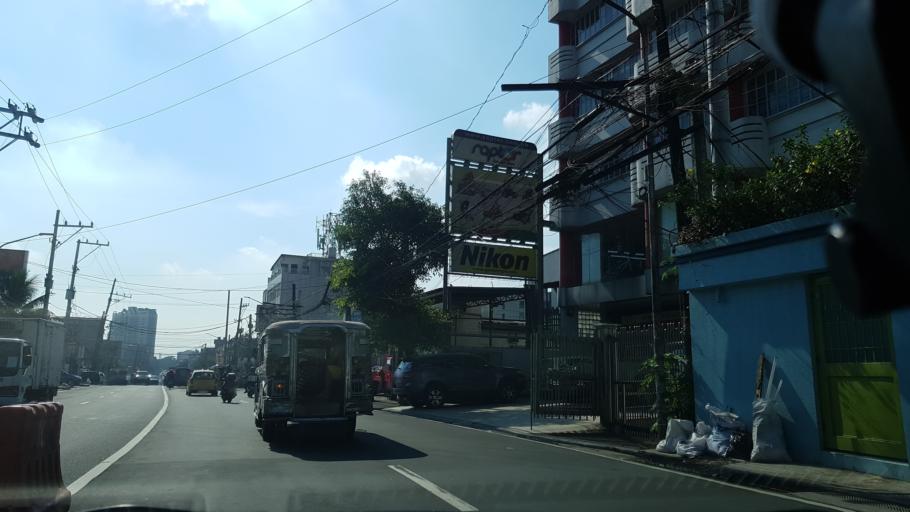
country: PH
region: Metro Manila
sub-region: San Juan
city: San Juan
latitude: 14.6247
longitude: 121.0412
